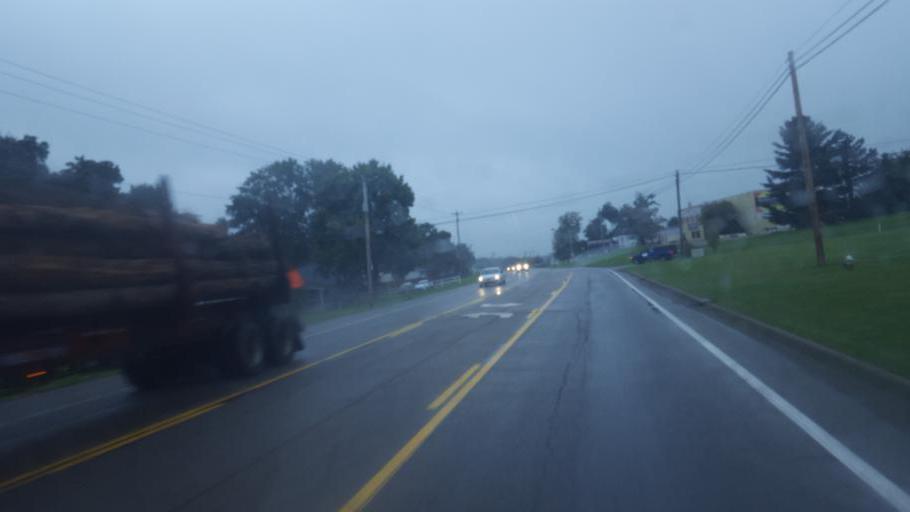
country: US
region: Ohio
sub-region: Jackson County
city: Jackson
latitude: 39.0262
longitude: -82.6210
